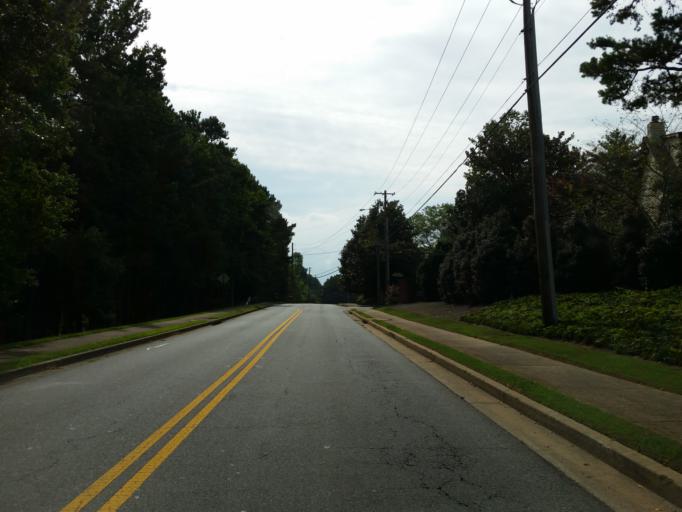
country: US
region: Georgia
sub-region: Cherokee County
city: Woodstock
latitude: 34.0407
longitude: -84.5011
